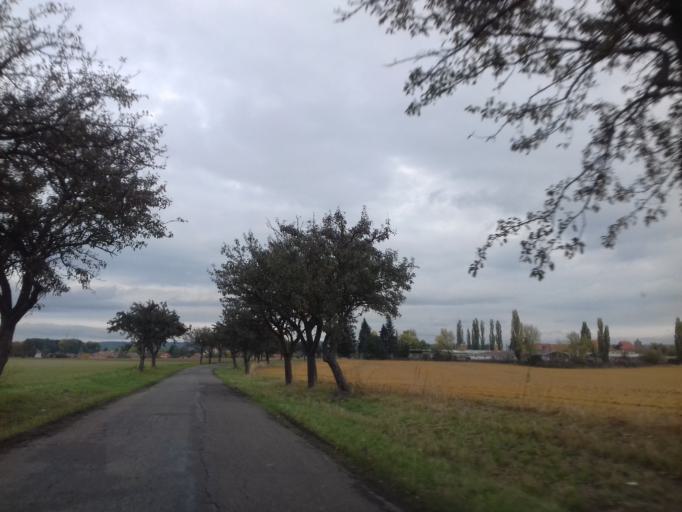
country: CZ
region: Pardubicky
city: Hrochuv Tynec
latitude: 49.9227
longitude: 15.9021
